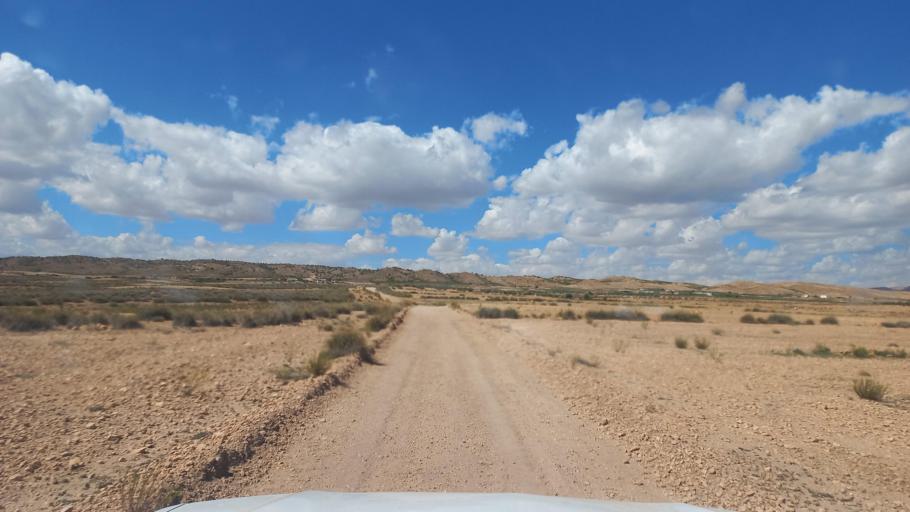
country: TN
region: Al Qasrayn
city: Sbiba
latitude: 35.3579
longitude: 9.0088
